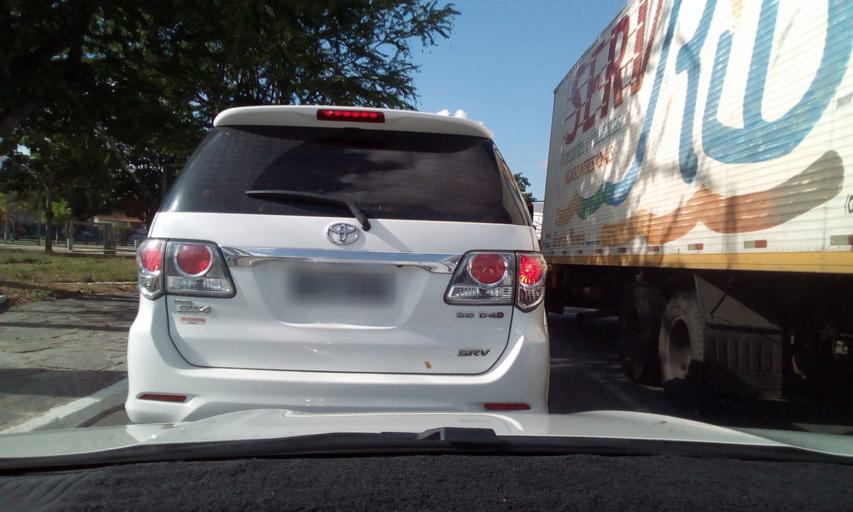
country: BR
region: Paraiba
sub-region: Campina Grande
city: Campina Grande
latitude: -7.2236
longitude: -35.8766
